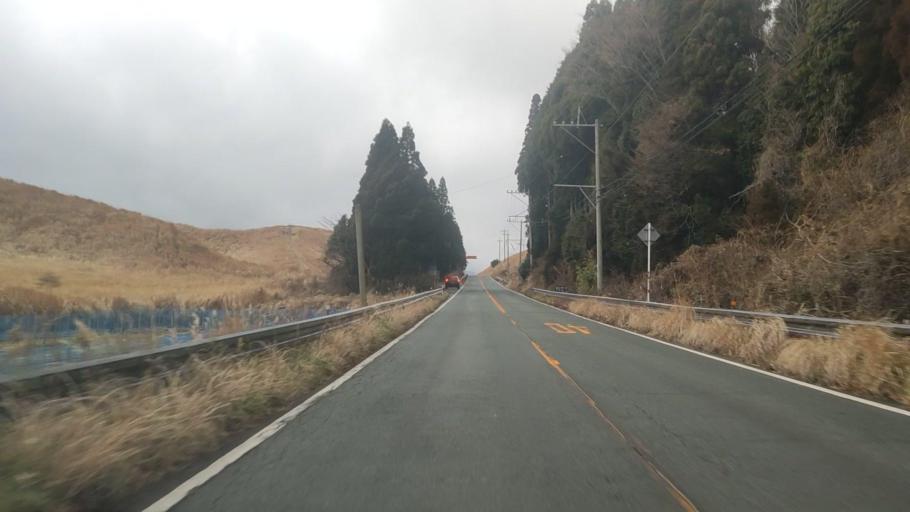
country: JP
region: Kumamoto
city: Aso
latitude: 32.9075
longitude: 131.1578
